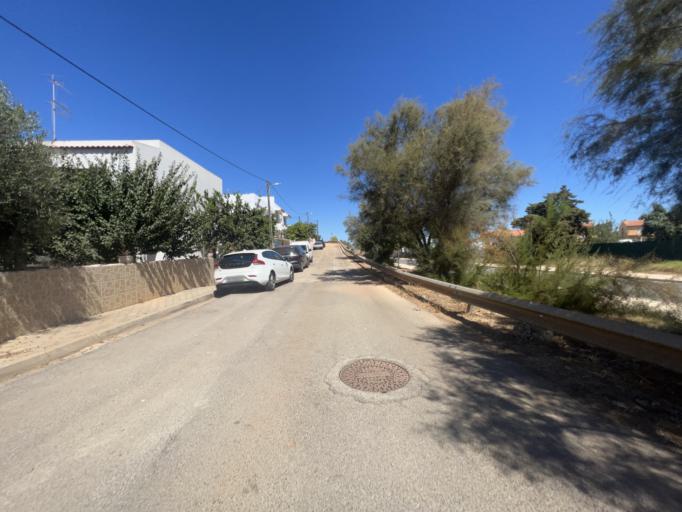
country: PT
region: Faro
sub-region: Portimao
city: Portimao
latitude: 37.1305
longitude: -8.5108
